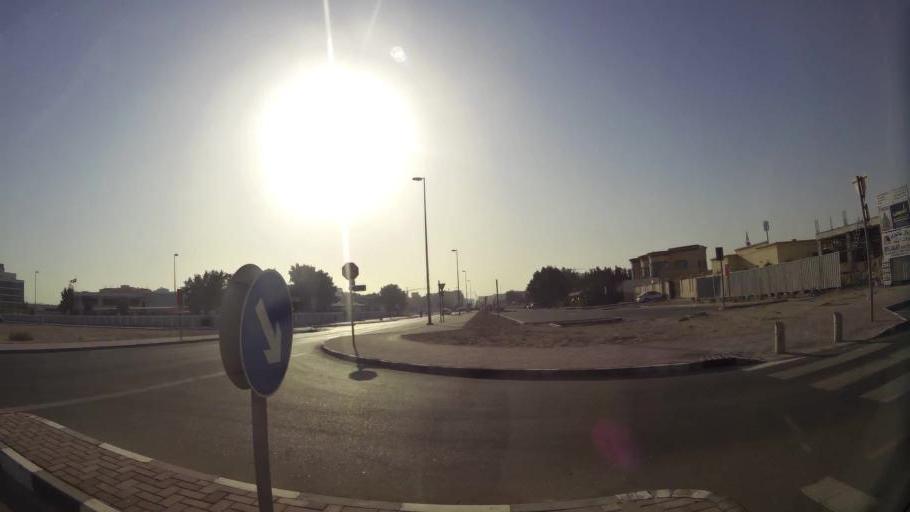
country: AE
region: Ash Shariqah
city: Sharjah
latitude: 25.2663
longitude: 55.3872
